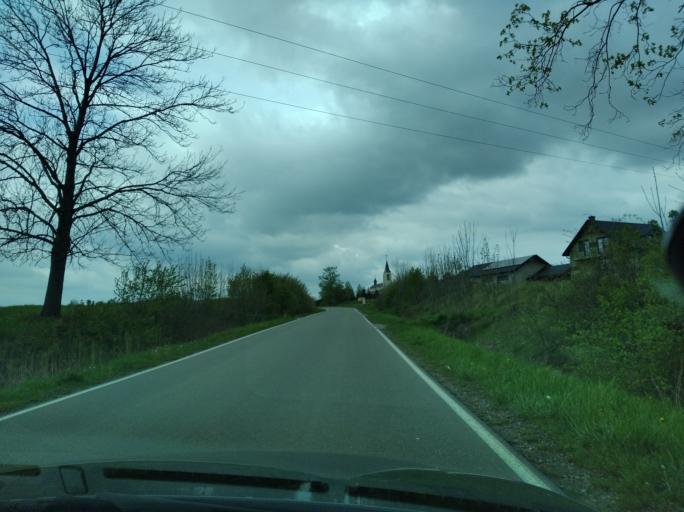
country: PL
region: Subcarpathian Voivodeship
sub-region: Powiat brzozowski
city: Turze Pole
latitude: 49.6368
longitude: 22.0034
